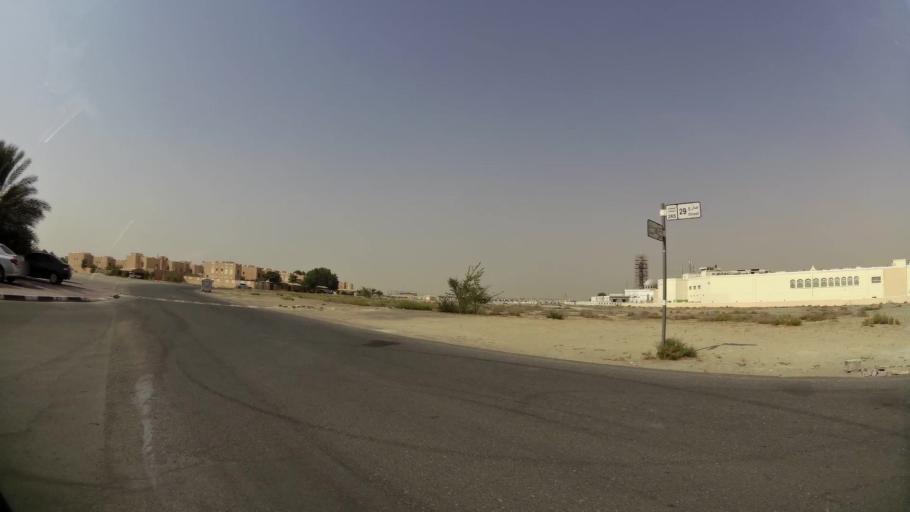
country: AE
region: Ash Shariqah
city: Sharjah
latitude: 25.2608
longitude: 55.4386
